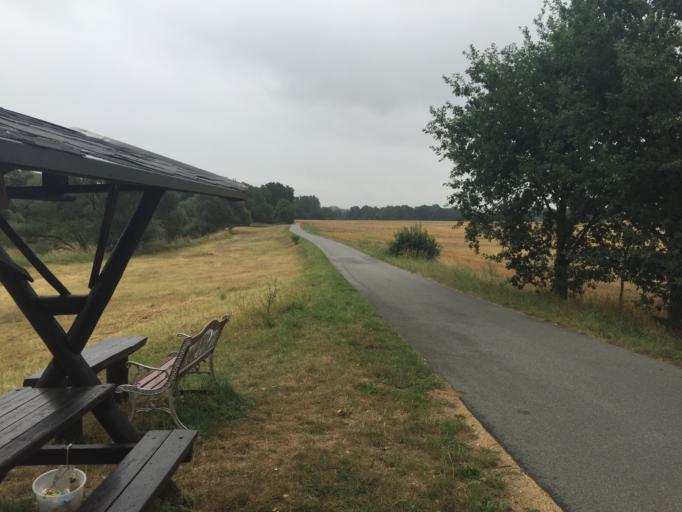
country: DE
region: Saxony
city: Rothenburg
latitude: 51.3348
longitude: 14.9807
